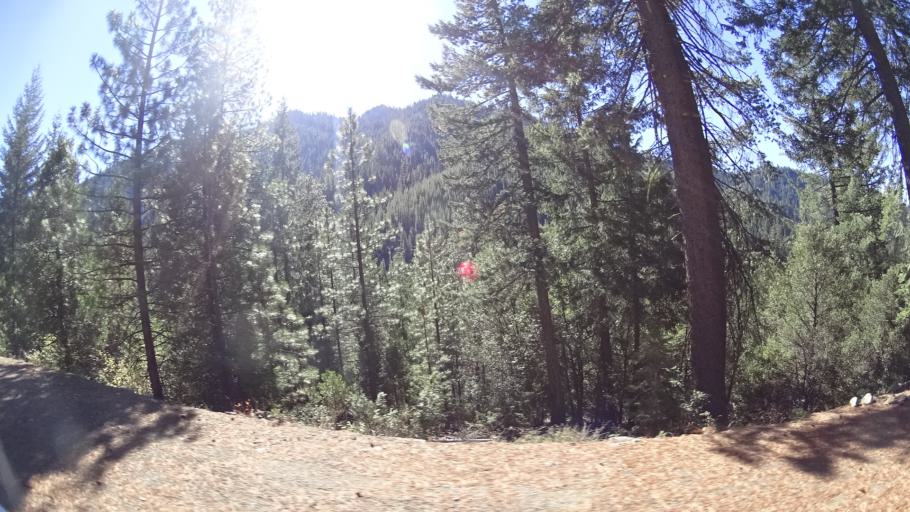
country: US
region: California
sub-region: Trinity County
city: Weaverville
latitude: 41.2261
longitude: -123.0032
